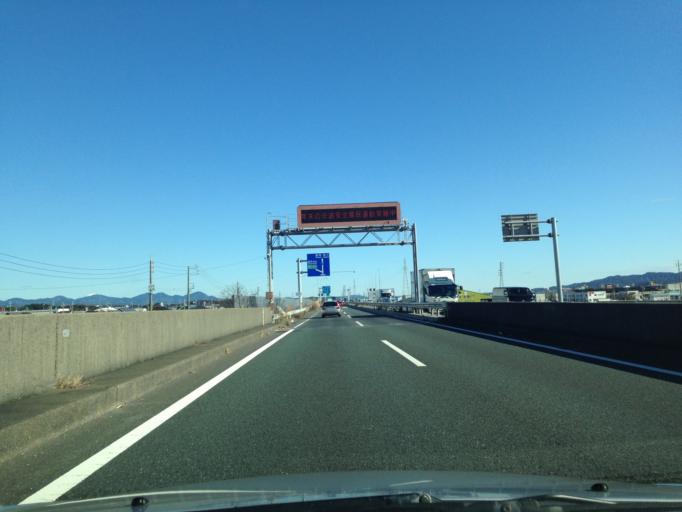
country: JP
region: Shizuoka
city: Fukuroi
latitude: 34.7497
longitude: 137.8990
